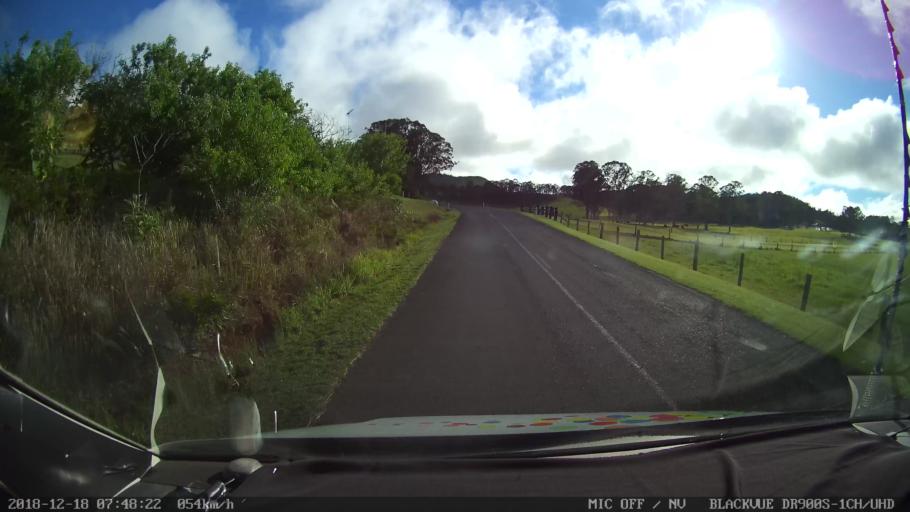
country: AU
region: New South Wales
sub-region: Kyogle
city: Kyogle
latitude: -28.4595
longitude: 152.5651
